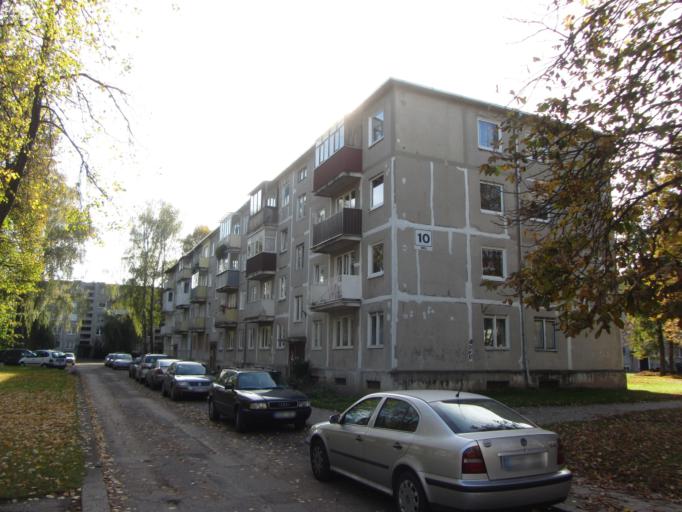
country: LT
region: Vilnius County
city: Elektrenai
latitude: 54.7867
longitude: 24.6624
